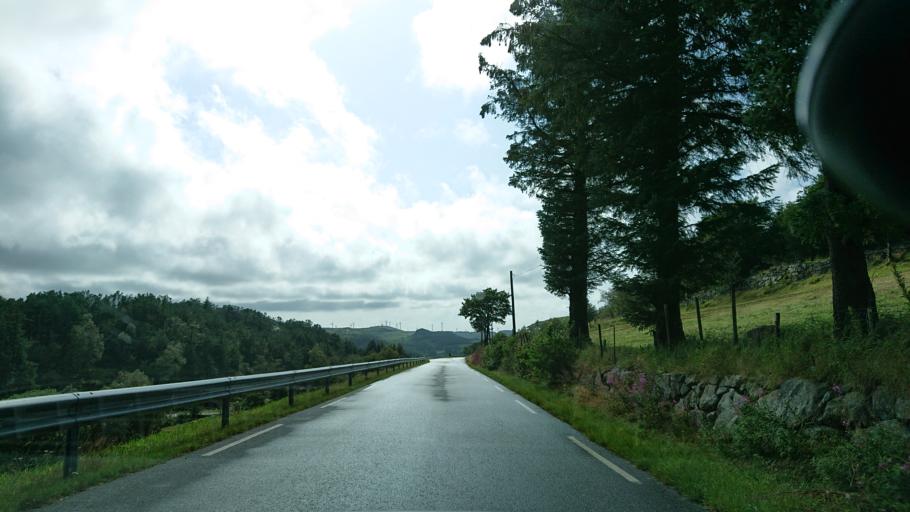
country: NO
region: Rogaland
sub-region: Gjesdal
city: Algard
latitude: 58.6818
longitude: 5.8582
